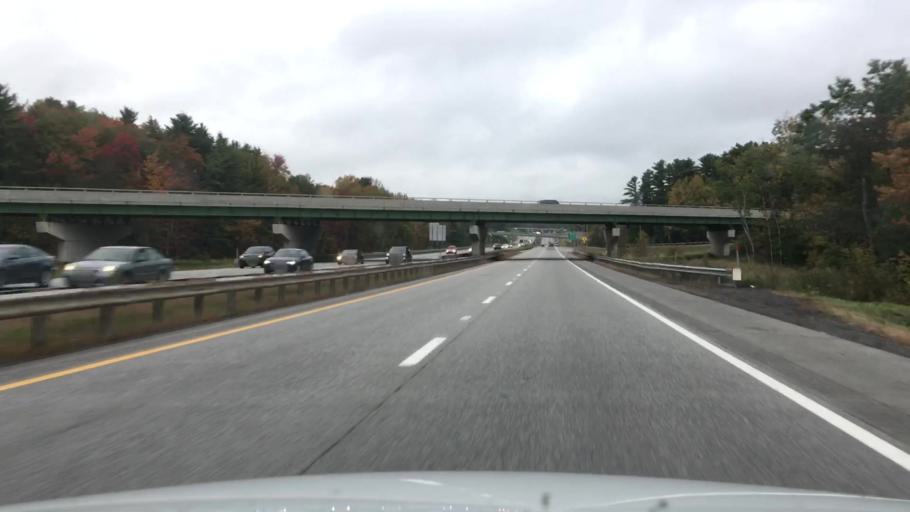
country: US
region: Maine
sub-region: Cumberland County
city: Falmouth
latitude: 43.7207
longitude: -70.3050
